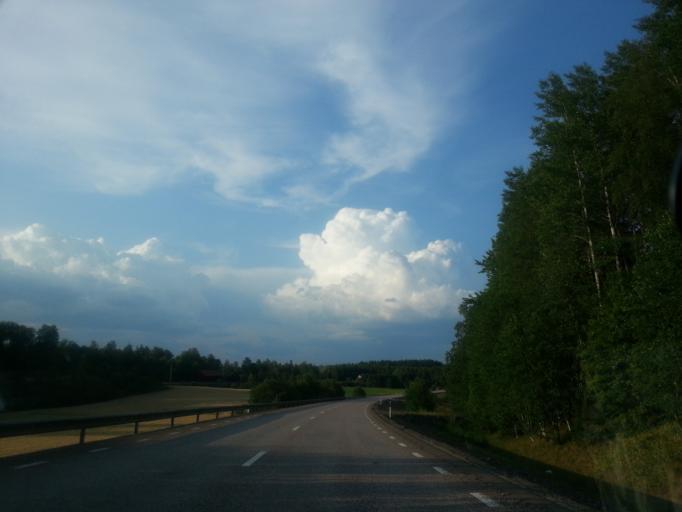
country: SE
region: Dalarna
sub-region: Avesta Kommun
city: Horndal
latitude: 60.2562
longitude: 16.3622
